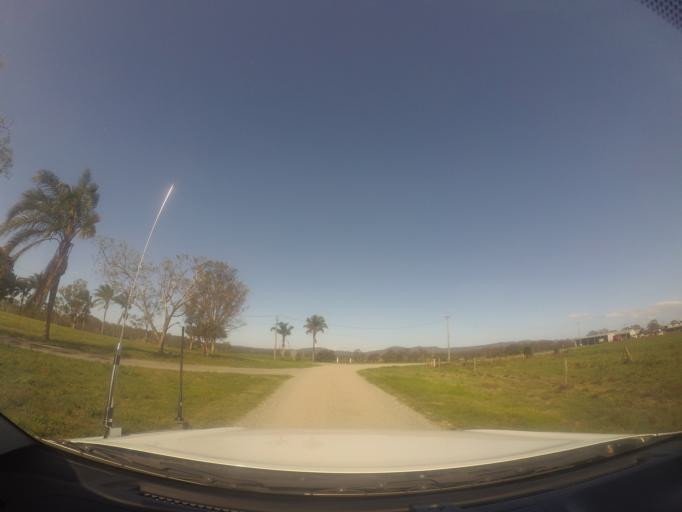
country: AU
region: Queensland
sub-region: Logan
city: Chambers Flat
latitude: -27.7514
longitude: 153.1000
